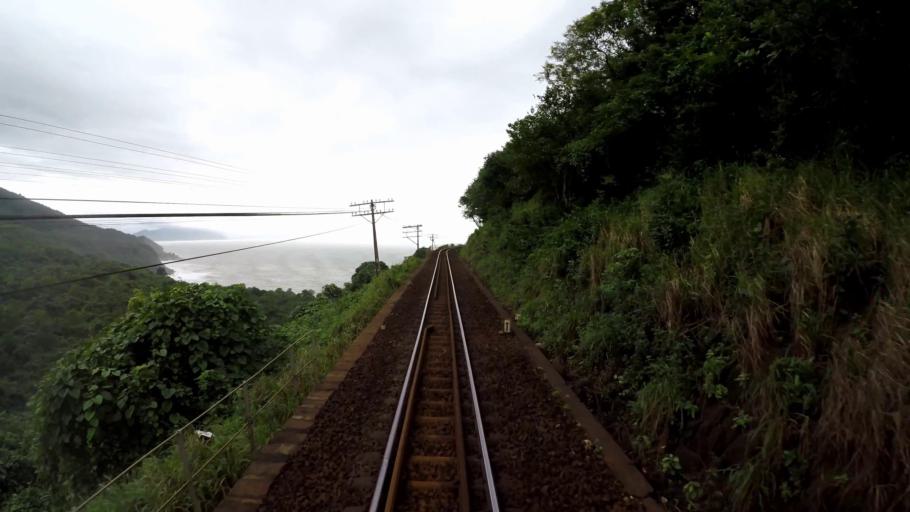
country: VN
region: Da Nang
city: Lien Chieu
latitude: 16.2084
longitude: 108.1228
